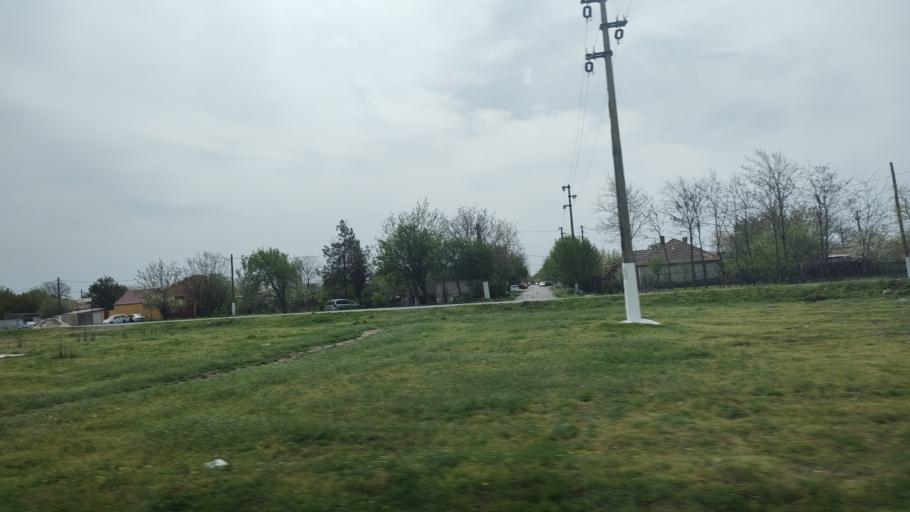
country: RO
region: Constanta
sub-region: Comuna Cobadin
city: Cobadin
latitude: 44.0702
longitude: 28.2217
